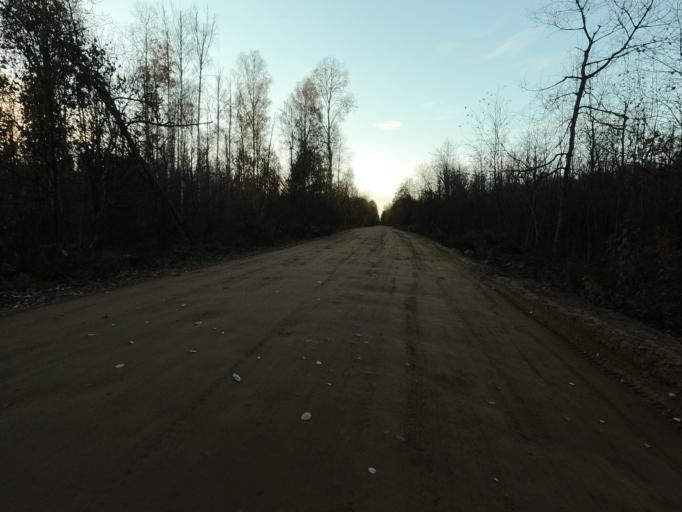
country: RU
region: Leningrad
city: Mga
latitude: 59.7560
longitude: 31.2768
